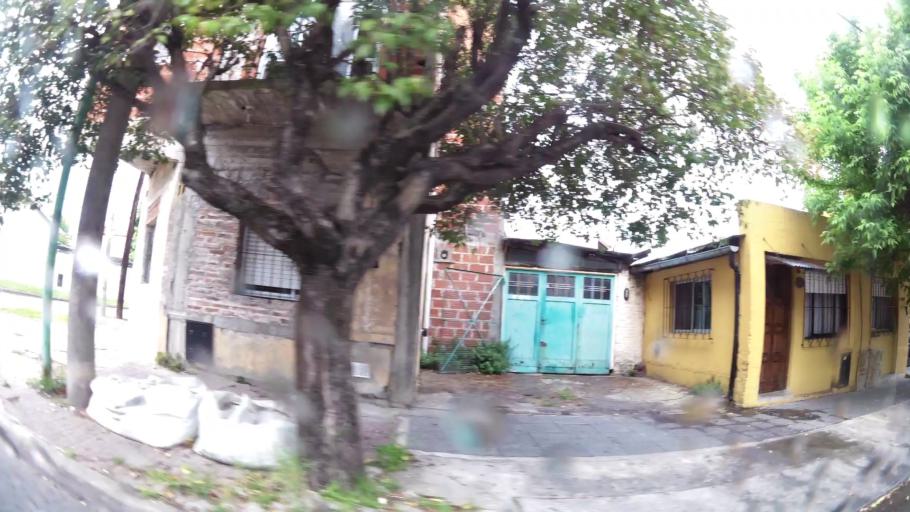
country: AR
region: Buenos Aires
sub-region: Partido de Quilmes
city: Quilmes
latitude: -34.7633
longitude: -58.2153
